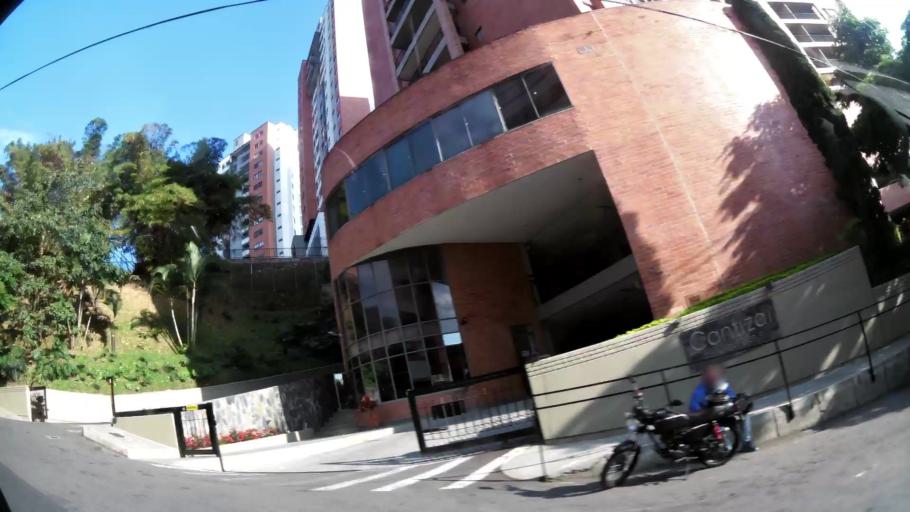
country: CO
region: Antioquia
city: Medellin
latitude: 6.2235
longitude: -75.5668
